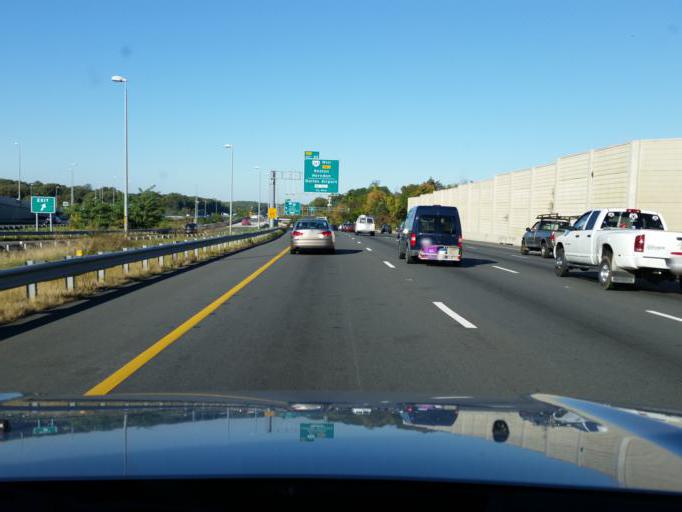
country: US
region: Virginia
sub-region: Fairfax County
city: Pimmit Hills
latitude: 38.9282
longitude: -77.2124
